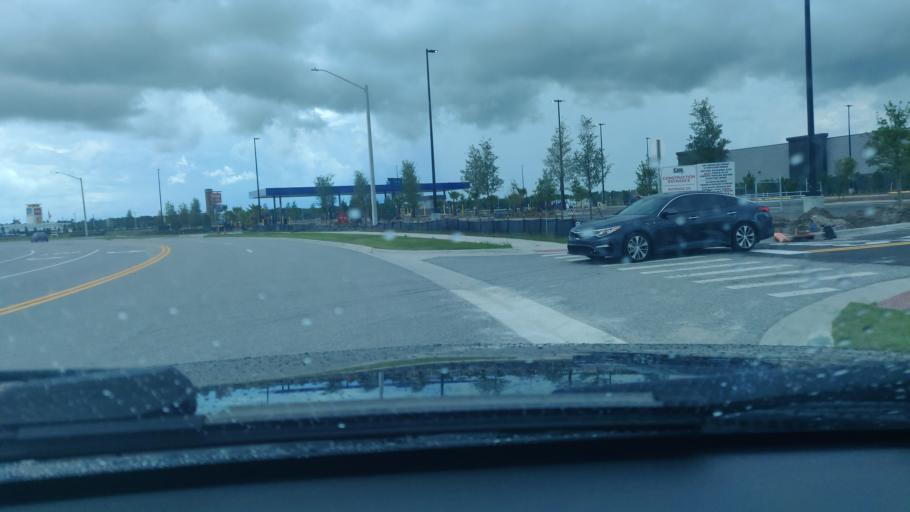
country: US
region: Florida
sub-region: Volusia County
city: Holly Hill
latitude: 29.2195
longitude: -81.0972
